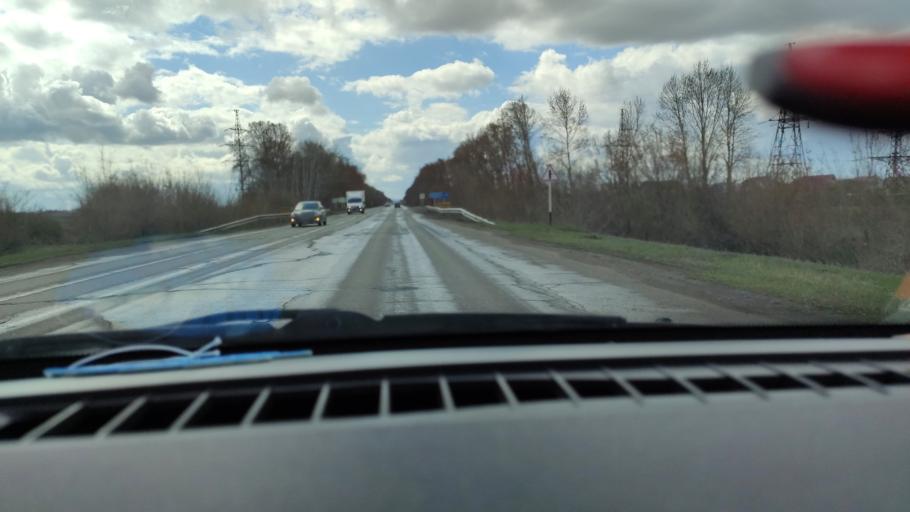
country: RU
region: Samara
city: Tol'yatti
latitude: 53.6281
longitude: 49.4166
